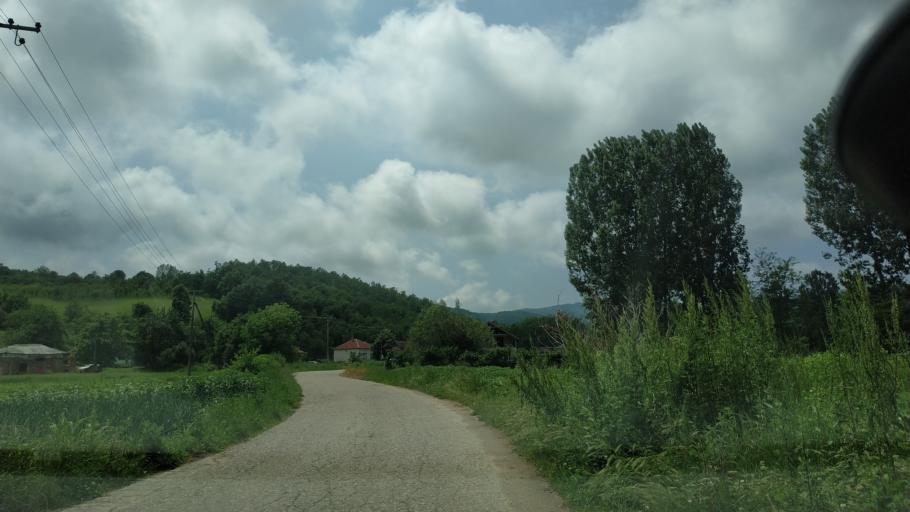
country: RS
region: Central Serbia
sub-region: Nisavski Okrug
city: Aleksinac
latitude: 43.4258
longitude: 21.7093
